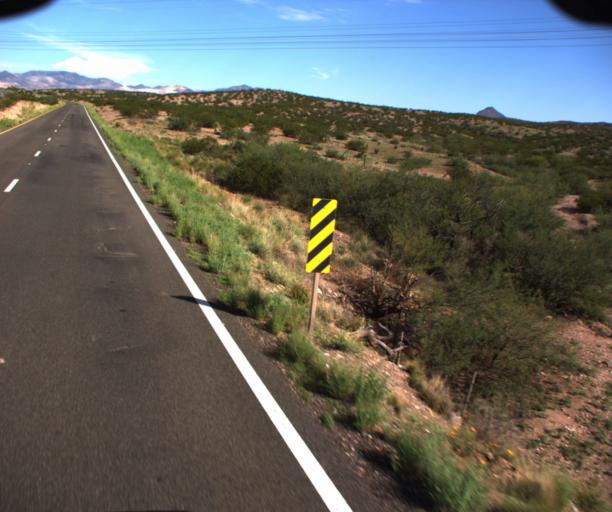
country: US
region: Arizona
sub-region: Greenlee County
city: Clifton
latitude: 32.9872
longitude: -109.2655
